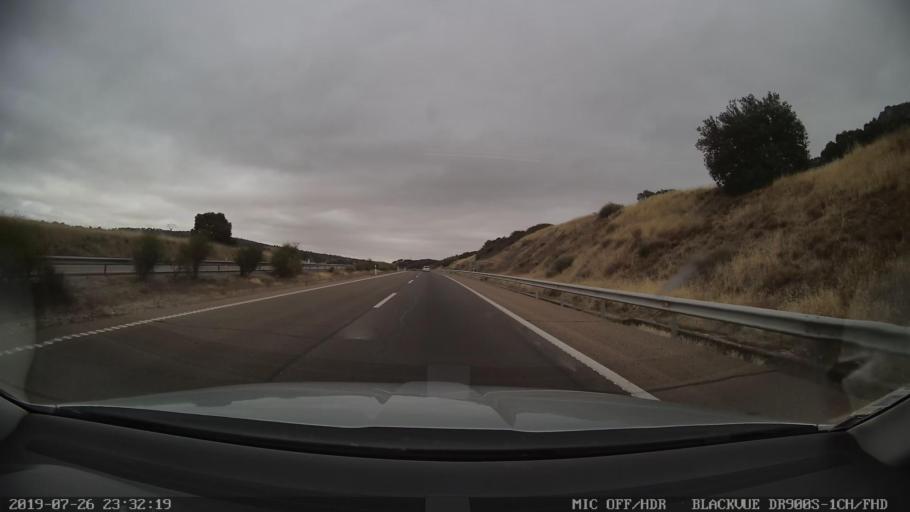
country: ES
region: Extremadura
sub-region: Provincia de Caceres
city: Puerto de Santa Cruz
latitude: 39.3166
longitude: -5.8562
